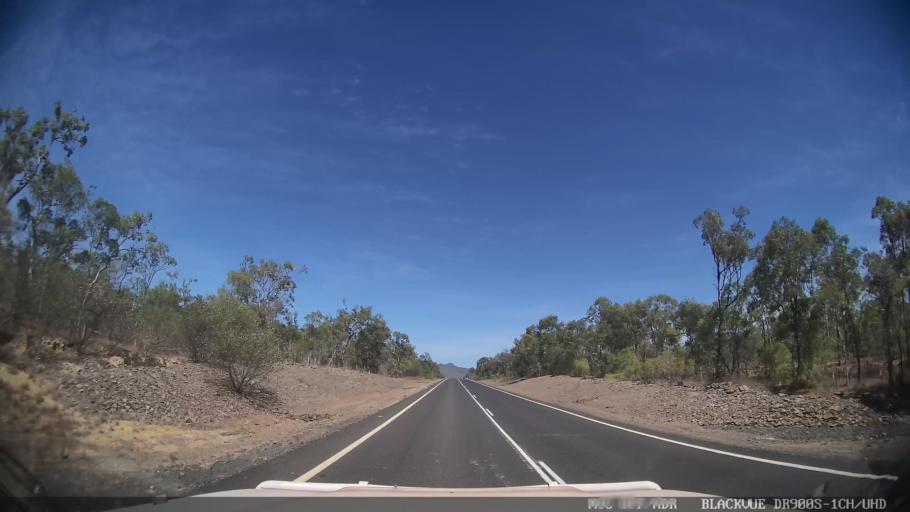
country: AU
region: Queensland
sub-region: Cook
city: Cooktown
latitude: -15.7028
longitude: 144.6076
